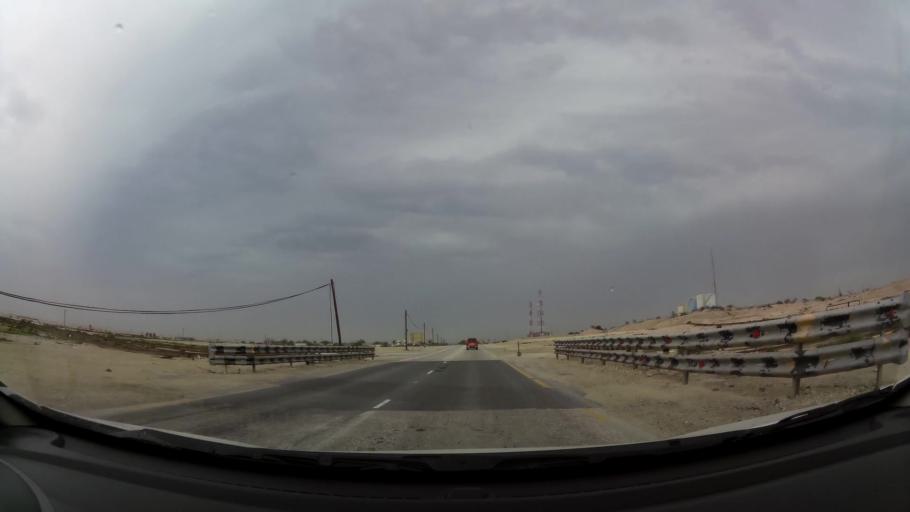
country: BH
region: Central Governorate
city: Dar Kulayb
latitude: 26.0766
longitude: 50.5506
